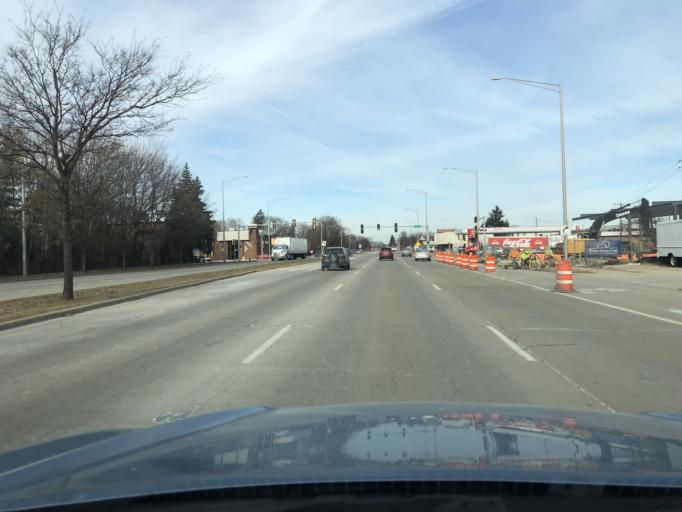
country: US
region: Illinois
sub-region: Cook County
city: Wheeling
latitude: 42.1553
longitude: -87.9156
